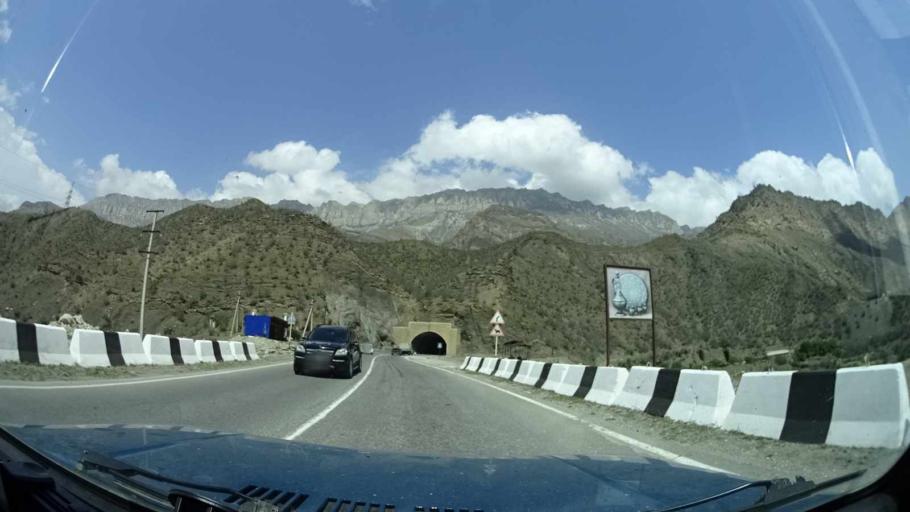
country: RU
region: Dagestan
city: Gimry
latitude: 42.7482
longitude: 46.8523
